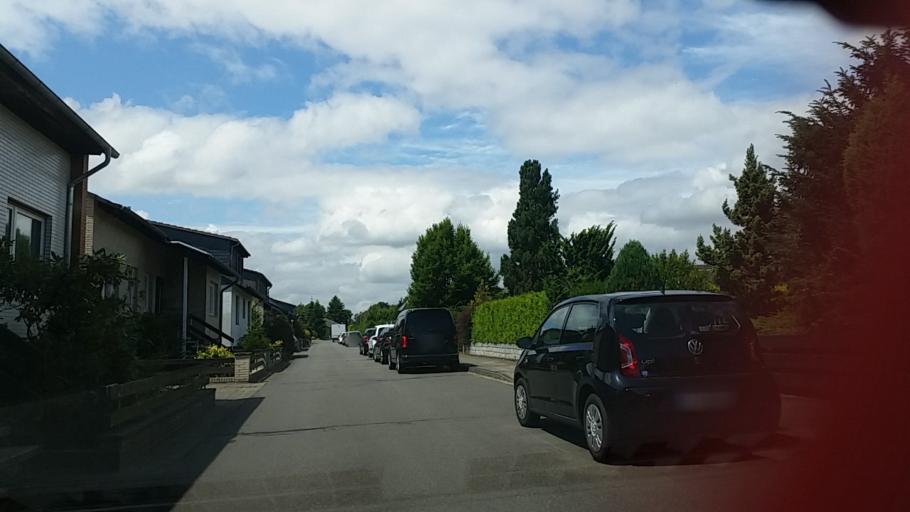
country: DE
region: Lower Saxony
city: Wolfsburg
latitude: 52.4232
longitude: 10.8227
